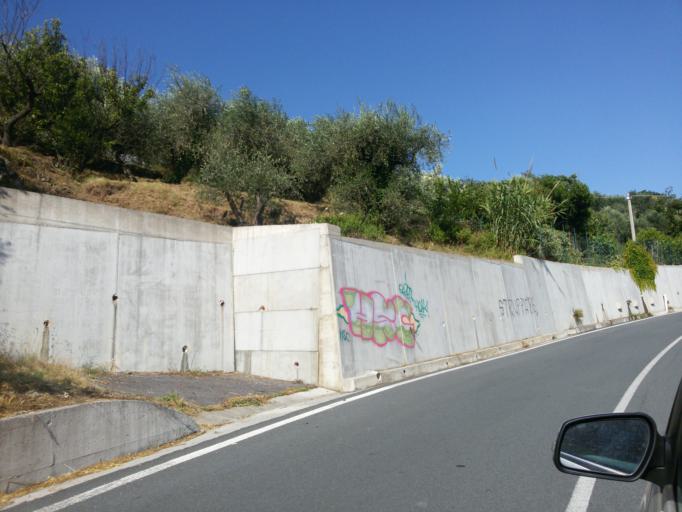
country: IT
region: Liguria
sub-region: Provincia di Savona
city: Borgio
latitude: 44.1811
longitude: 8.3021
